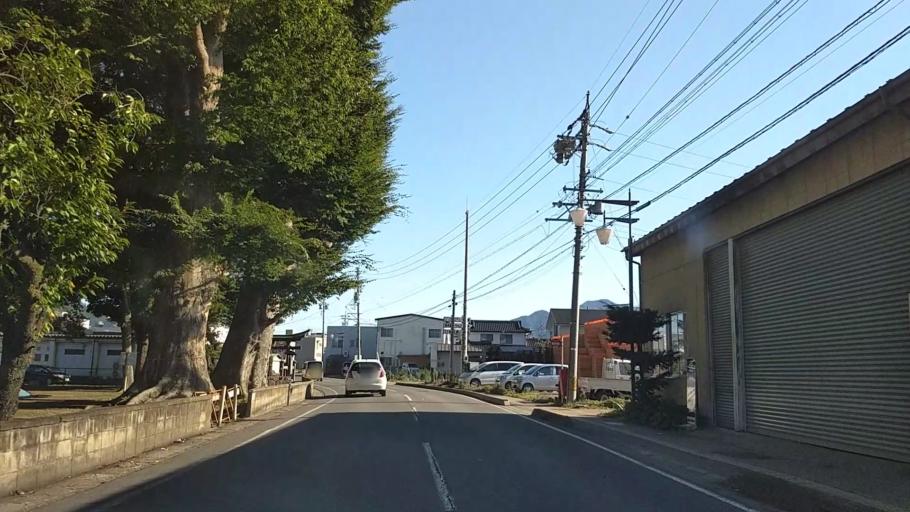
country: JP
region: Nagano
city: Nagano-shi
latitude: 36.5333
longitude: 138.1206
